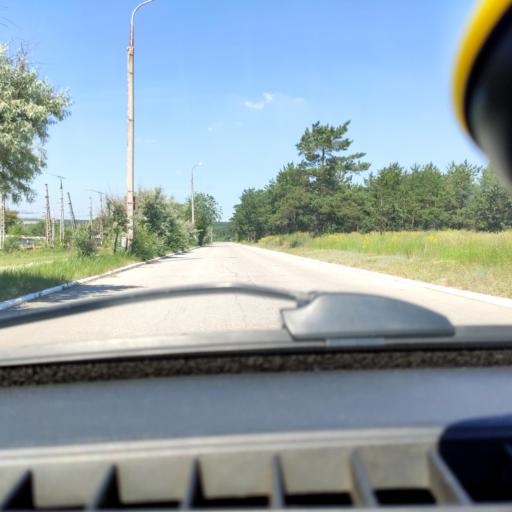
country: RU
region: Samara
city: Zhigulevsk
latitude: 53.4900
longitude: 49.5153
